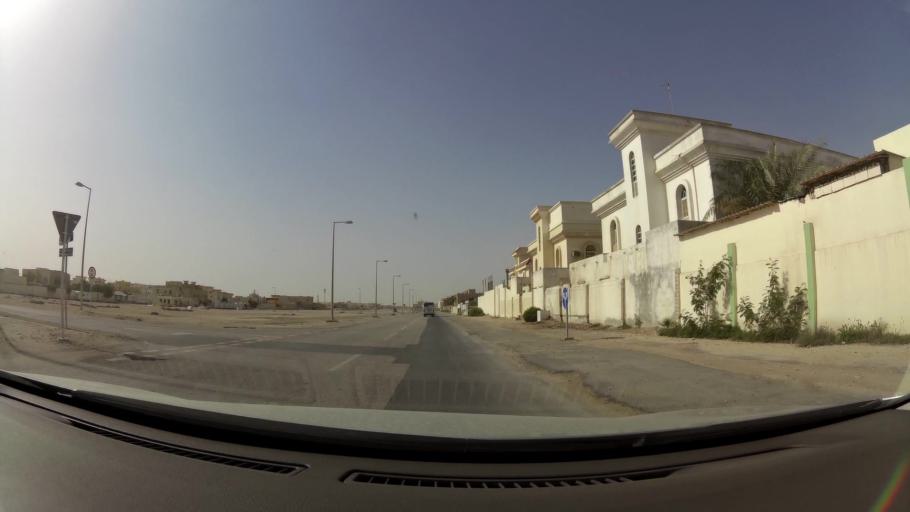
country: QA
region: Baladiyat ar Rayyan
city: Ar Rayyan
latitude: 25.3485
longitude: 51.4510
